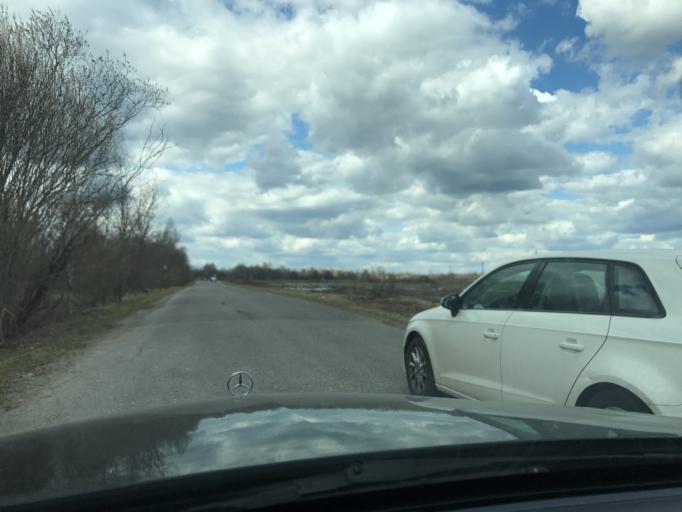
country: RU
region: Vladimir
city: Pokrov
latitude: 55.8875
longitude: 39.2356
